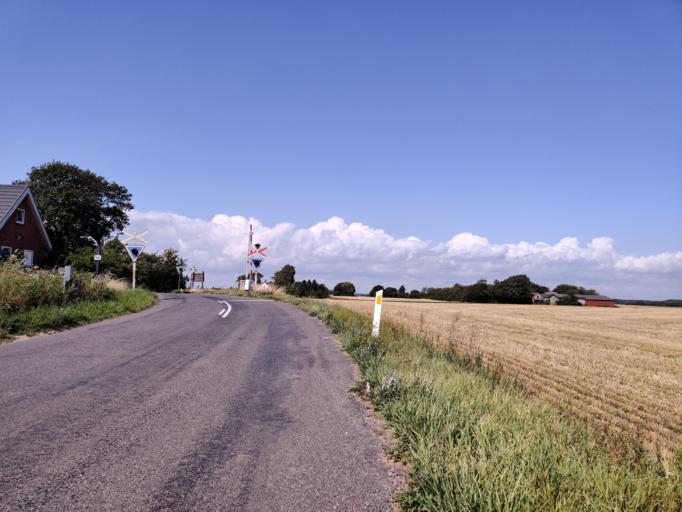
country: DK
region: Zealand
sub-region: Guldborgsund Kommune
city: Nykobing Falster
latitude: 54.6140
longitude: 11.9185
